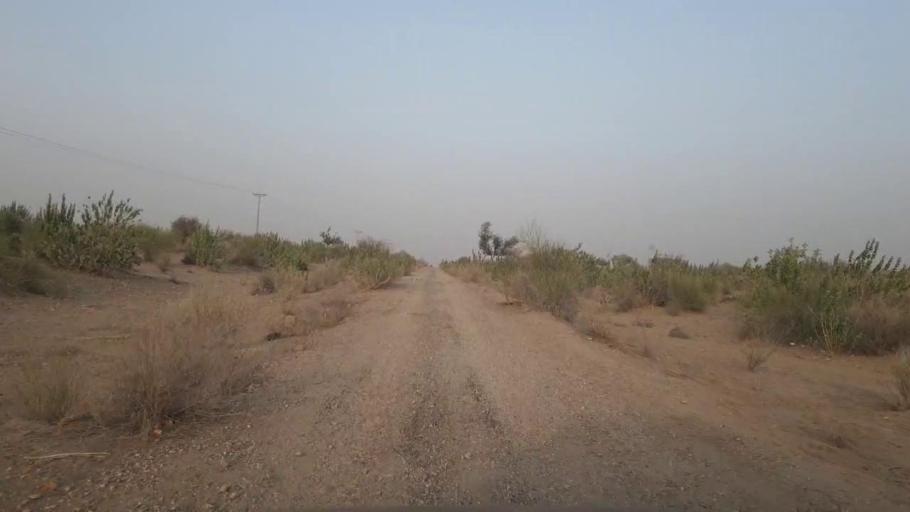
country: PK
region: Sindh
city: Chor
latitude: 25.5302
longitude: 69.9530
